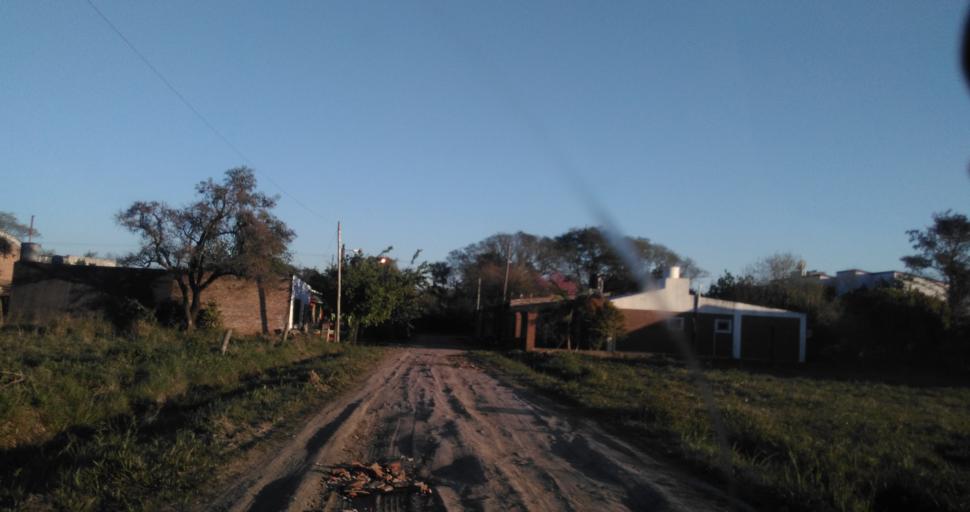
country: AR
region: Chaco
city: Fontana
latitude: -27.4290
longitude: -59.0337
